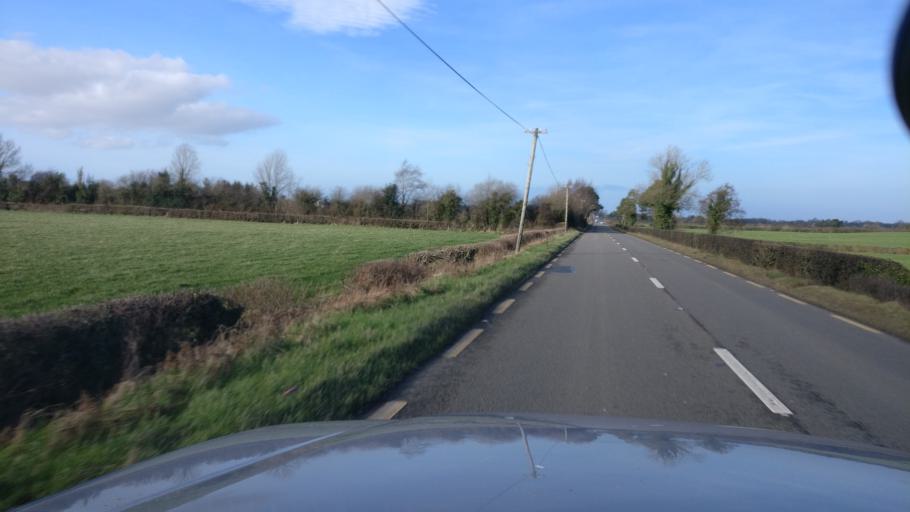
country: IE
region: Leinster
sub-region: Laois
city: Mountmellick
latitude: 53.0871
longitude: -7.3338
